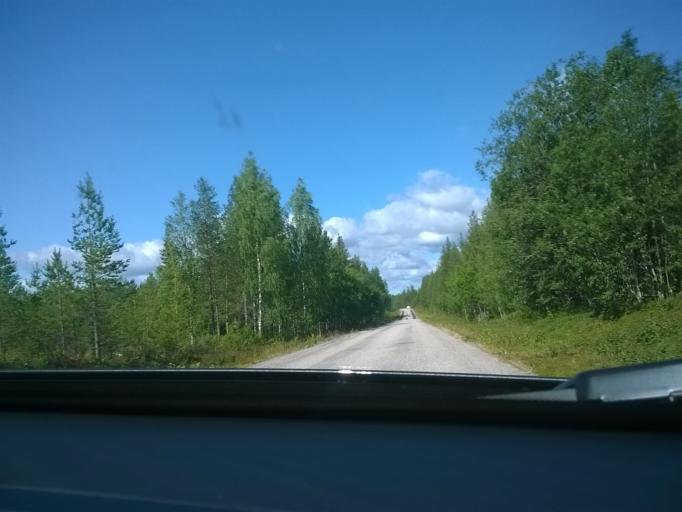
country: FI
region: Kainuu
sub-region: Kehys-Kainuu
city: Kuhmo
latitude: 64.4577
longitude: 29.6448
